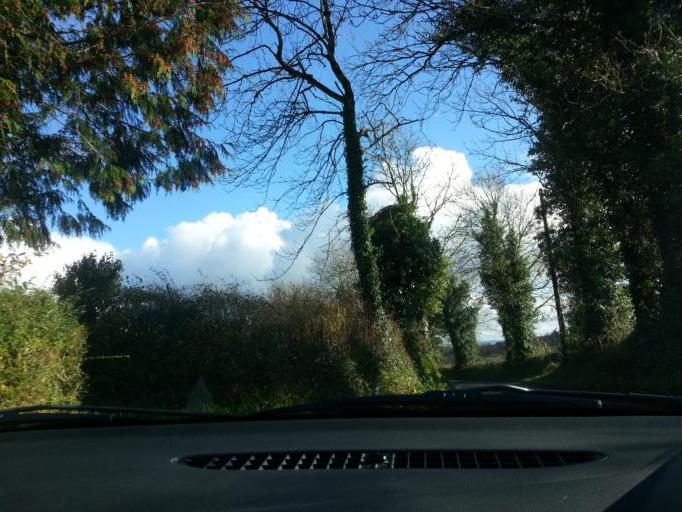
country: IE
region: Ulster
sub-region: County Monaghan
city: Clones
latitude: 54.2309
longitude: -7.2870
